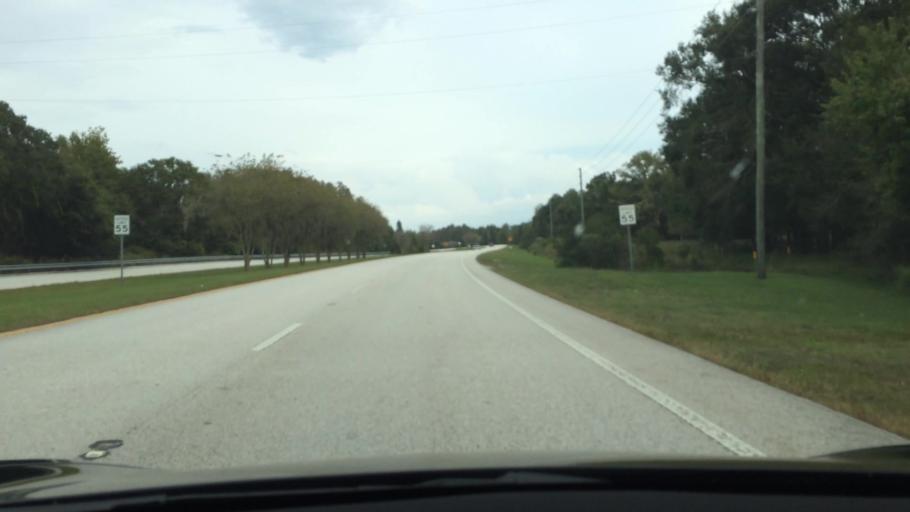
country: US
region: Florida
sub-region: Pasco County
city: Trinity
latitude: 28.1704
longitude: -82.6828
